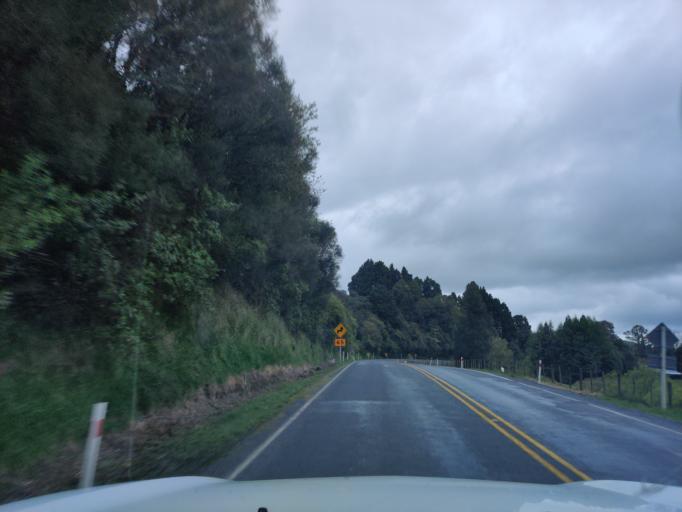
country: NZ
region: Waikato
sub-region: Otorohanga District
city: Otorohanga
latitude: -38.6106
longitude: 175.2176
